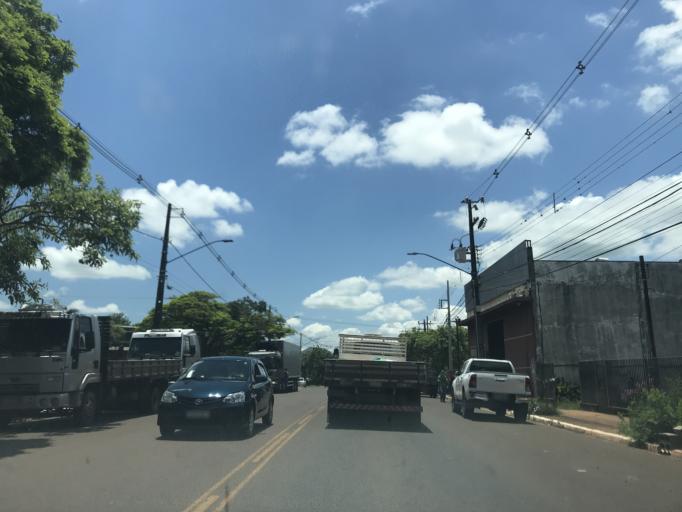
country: BR
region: Parana
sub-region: Marialva
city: Marialva
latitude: -23.4911
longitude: -51.7861
